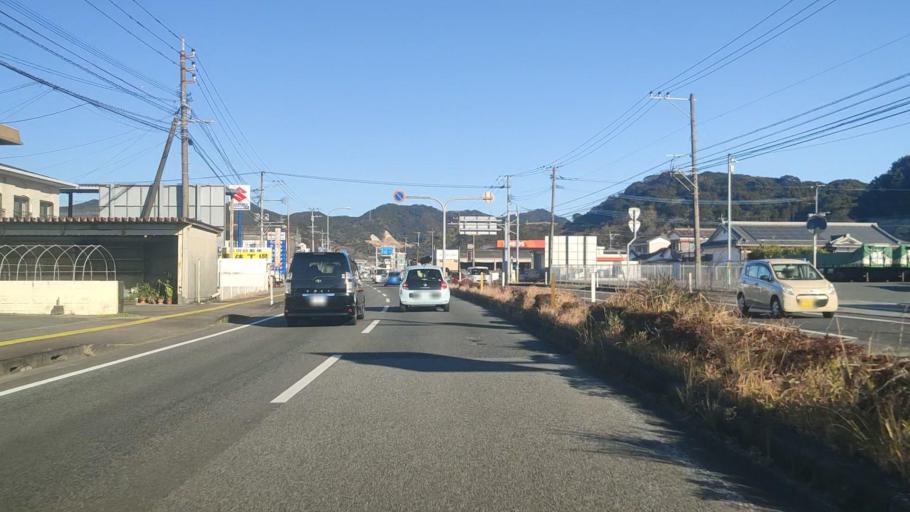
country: JP
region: Miyazaki
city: Nobeoka
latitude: 32.4890
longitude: 131.6643
